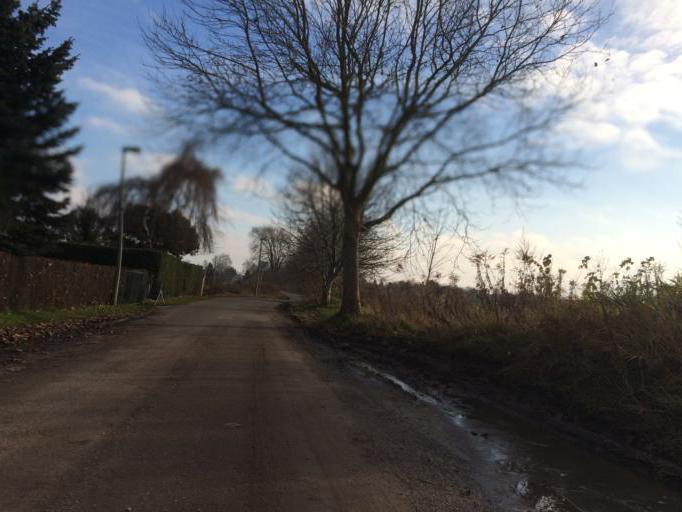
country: DE
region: Berlin
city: Blankenburg
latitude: 52.6054
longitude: 13.4643
